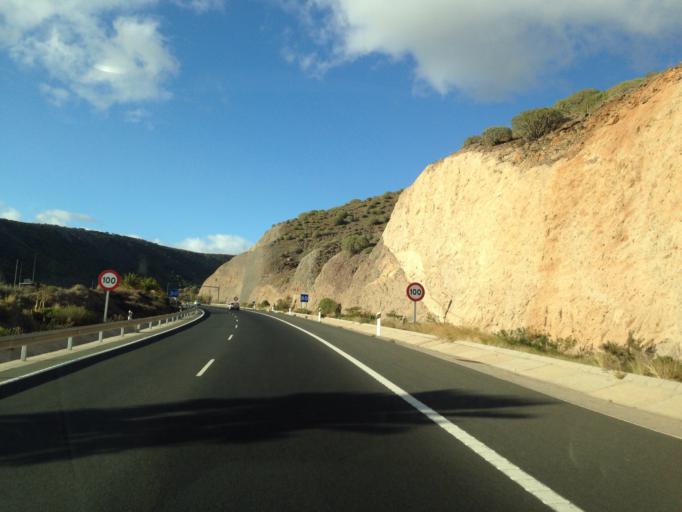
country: ES
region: Canary Islands
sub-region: Provincia de Las Palmas
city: Puerto Rico
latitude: 27.7804
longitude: -15.6772
